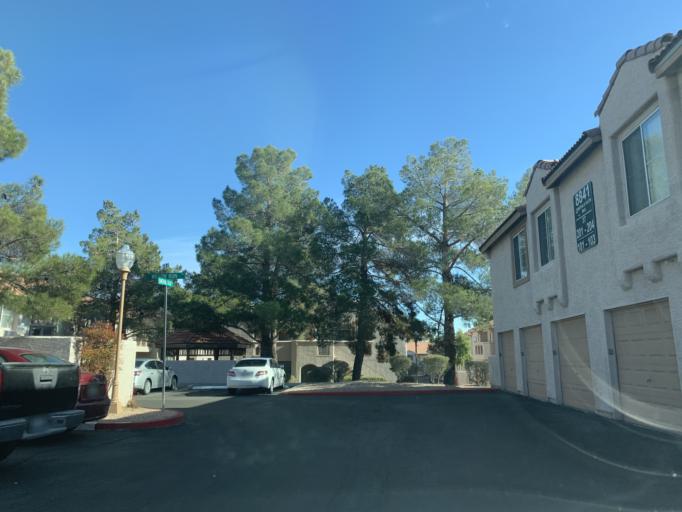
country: US
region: Nevada
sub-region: Clark County
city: Summerlin South
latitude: 36.1306
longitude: -115.2926
